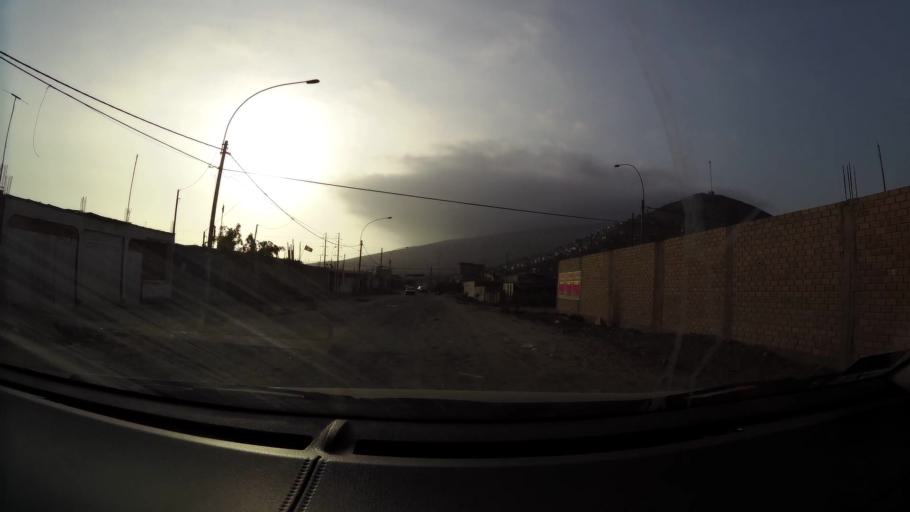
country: PE
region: Lima
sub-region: Lima
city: Santa Rosa
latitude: -11.7457
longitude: -77.1482
